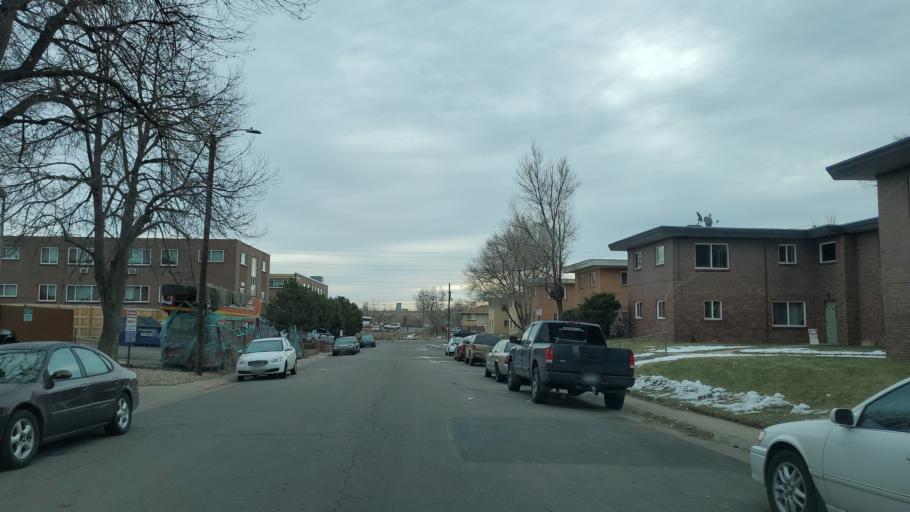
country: US
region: Colorado
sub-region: Denver County
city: Denver
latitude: 39.6958
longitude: -105.0082
